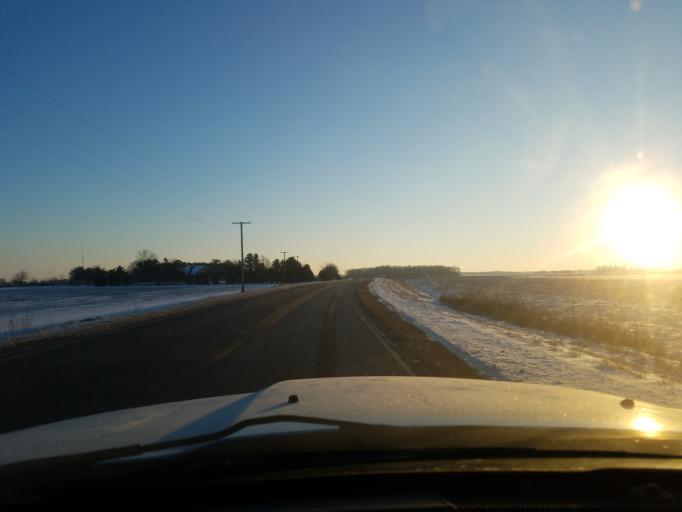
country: US
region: Indiana
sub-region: Marshall County
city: Bremen
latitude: 41.4498
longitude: -86.2182
